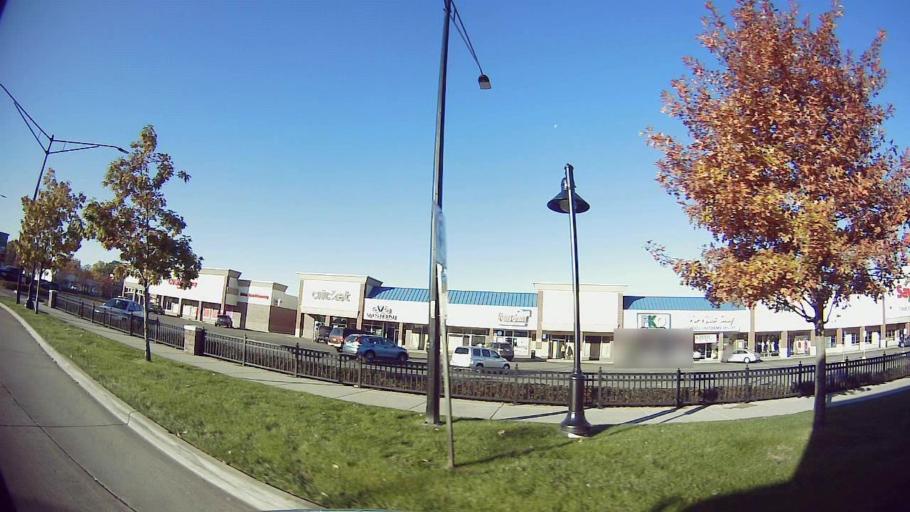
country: US
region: Michigan
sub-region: Oakland County
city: Oak Park
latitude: 42.4609
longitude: -83.1821
